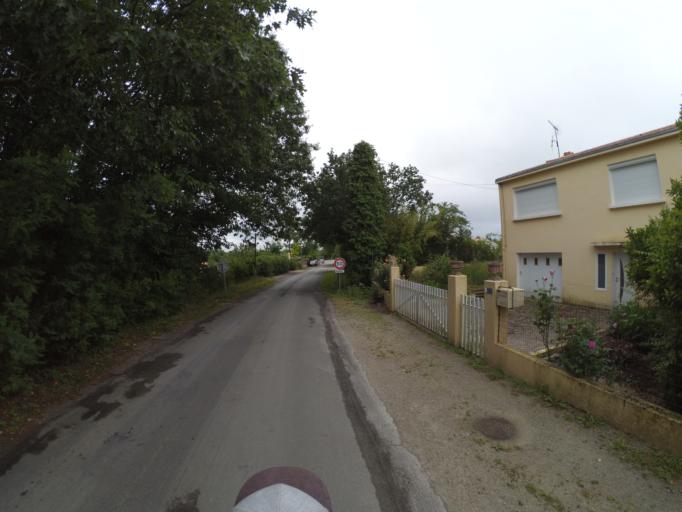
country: FR
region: Pays de la Loire
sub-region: Departement de la Vendee
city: La Roche-sur-Yon
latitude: 46.6350
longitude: -1.4290
